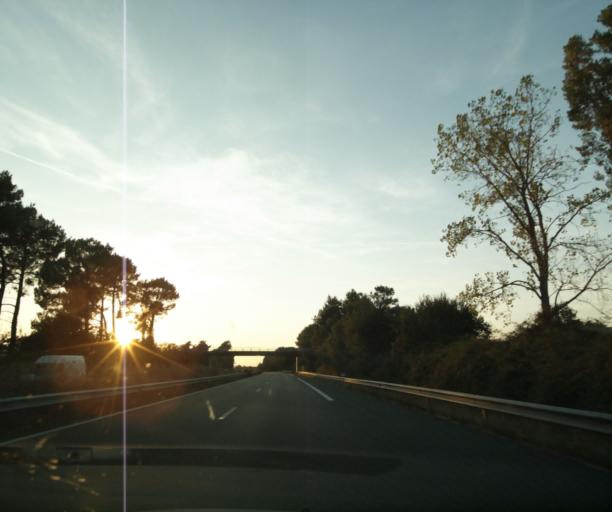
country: FR
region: Aquitaine
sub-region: Departement du Lot-et-Garonne
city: Fourques-sur-Garonne
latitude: 44.4250
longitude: 0.1623
